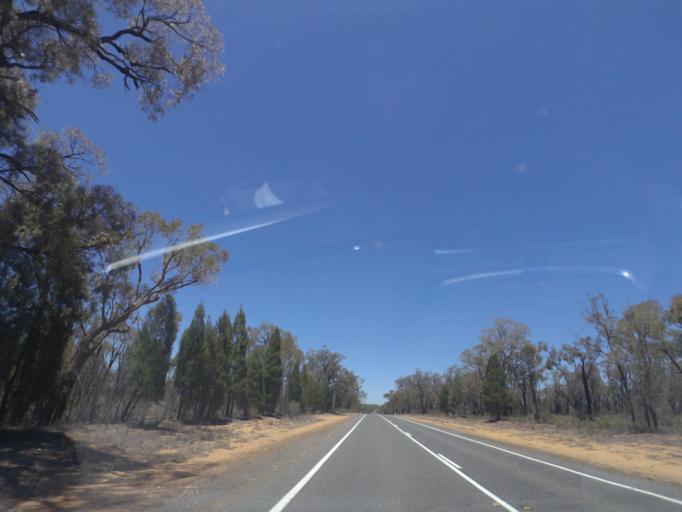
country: AU
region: New South Wales
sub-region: Narrabri
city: Narrabri
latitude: -30.7151
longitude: 149.5281
